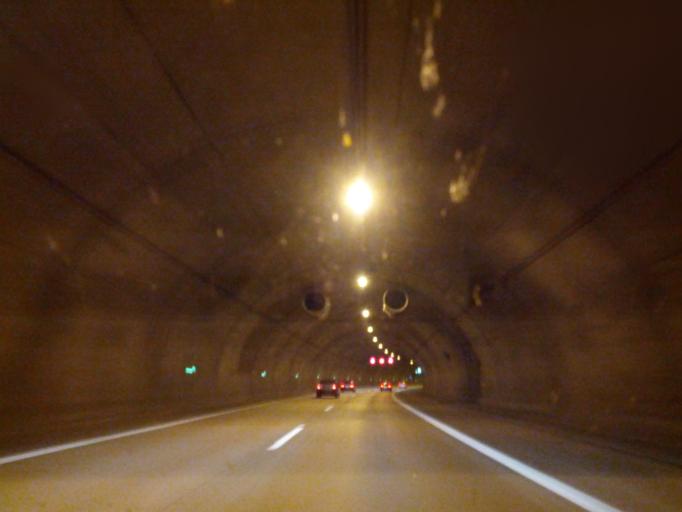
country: DE
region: Saxony
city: Freital
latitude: 51.0277
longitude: 13.6778
